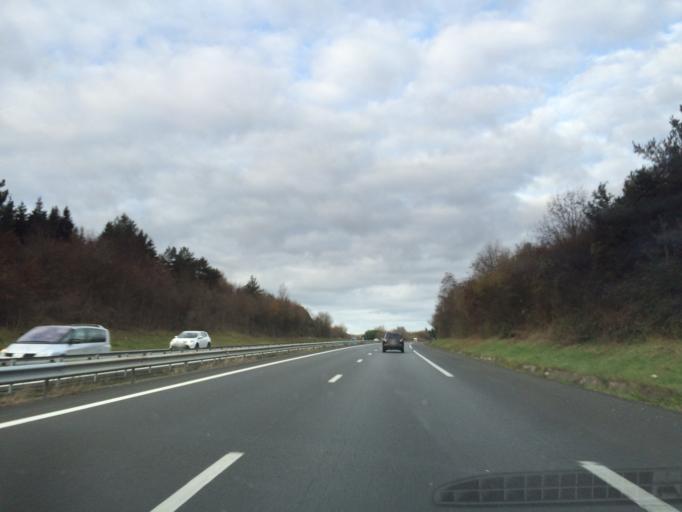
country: FR
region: Poitou-Charentes
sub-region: Departement de la Charente-Maritime
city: Saint-Jean-d'Angely
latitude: 46.0177
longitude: -0.5415
